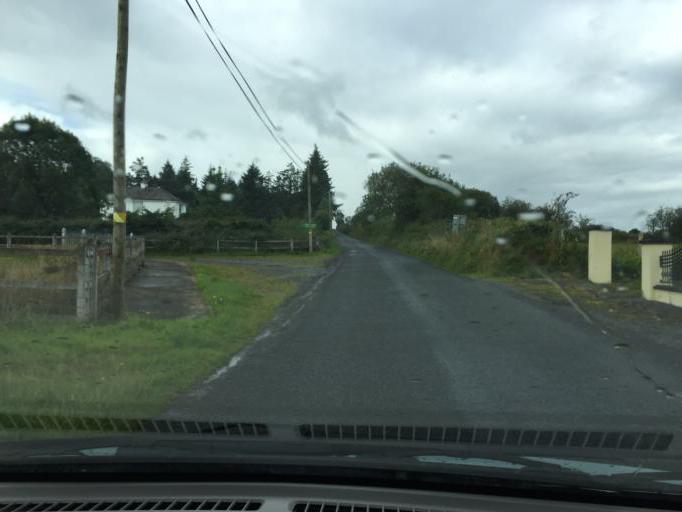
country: IE
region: Connaught
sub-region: Sligo
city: Tobercurry
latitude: 54.0382
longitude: -8.8456
